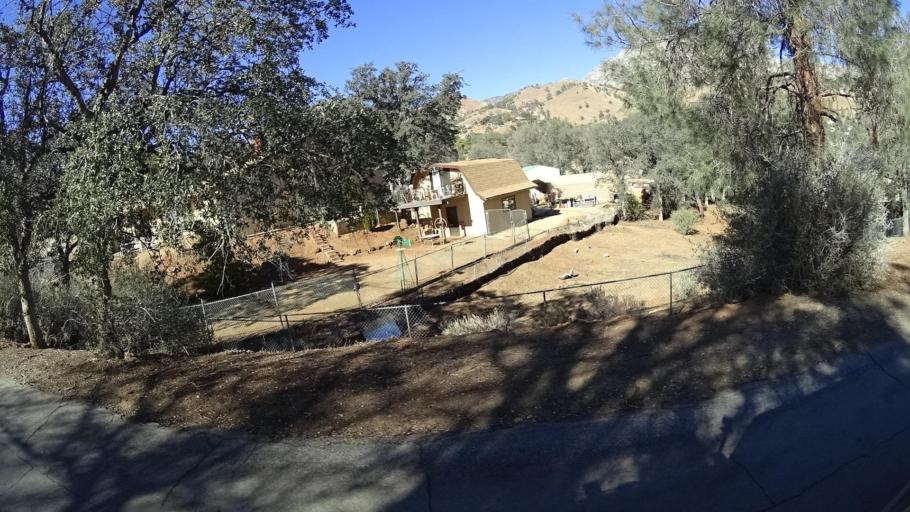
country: US
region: California
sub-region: Kern County
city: Wofford Heights
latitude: 35.7081
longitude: -118.4722
